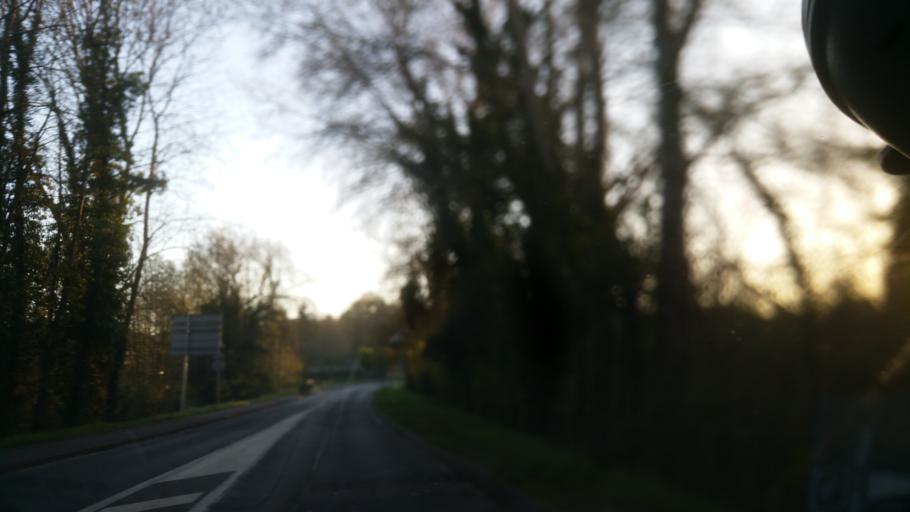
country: FR
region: Ile-de-France
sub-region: Departement de l'Essonne
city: Saint-Cyr-sous-Dourdan
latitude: 48.5688
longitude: 2.0323
